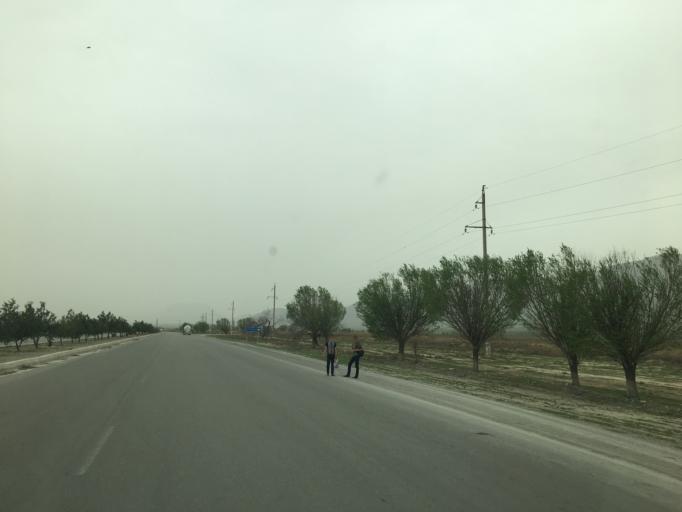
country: TM
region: Ahal
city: Arcabil
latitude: 38.2012
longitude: 57.8253
